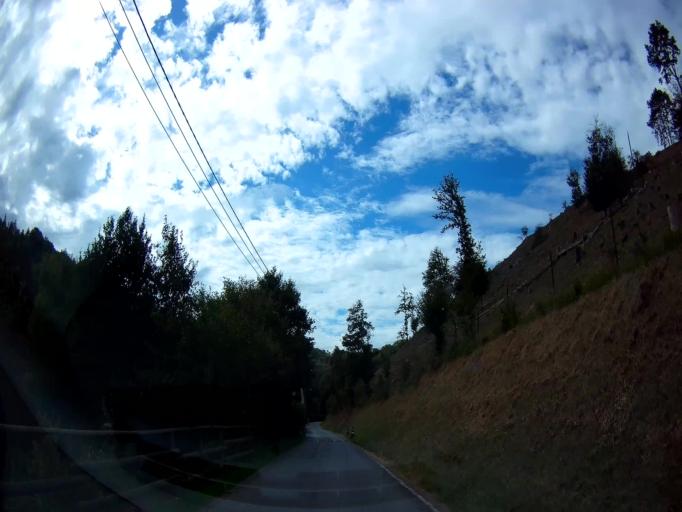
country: BE
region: Wallonia
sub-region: Province de Liege
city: Hamoir
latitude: 50.3933
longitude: 5.5417
